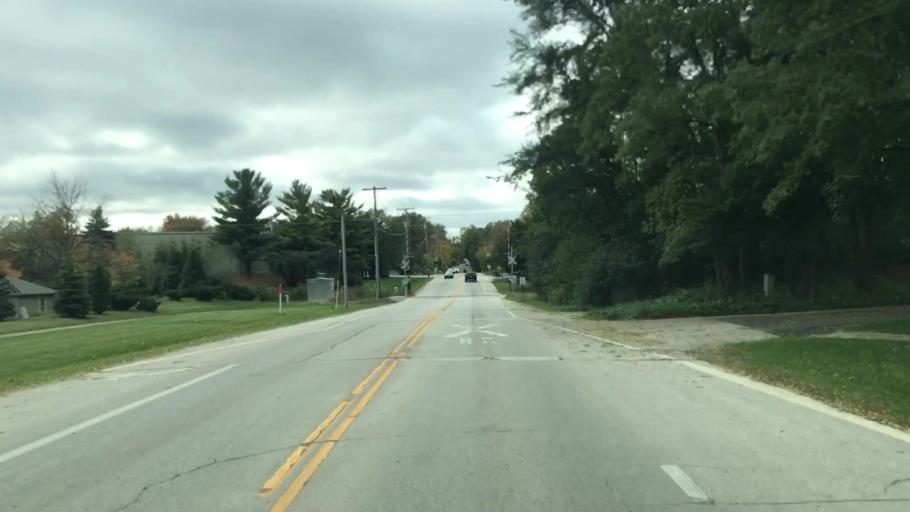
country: US
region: Wisconsin
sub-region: Waukesha County
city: Brookfield
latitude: 43.0700
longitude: -88.1260
